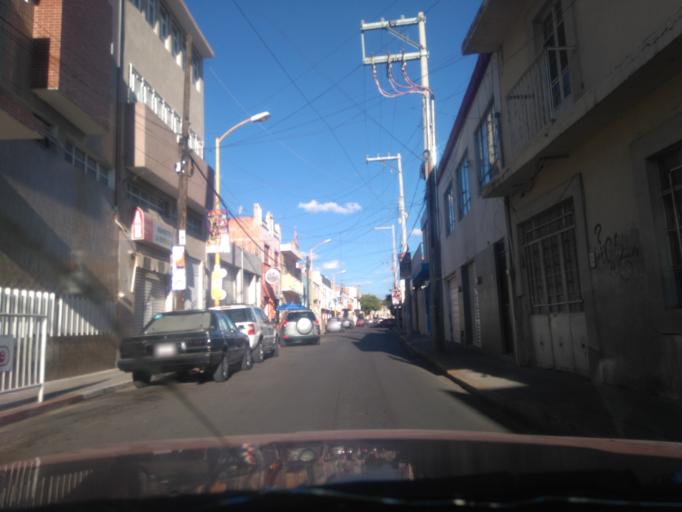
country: MX
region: Aguascalientes
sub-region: Aguascalientes
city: Aguascalientes
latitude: 21.8782
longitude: -102.3029
